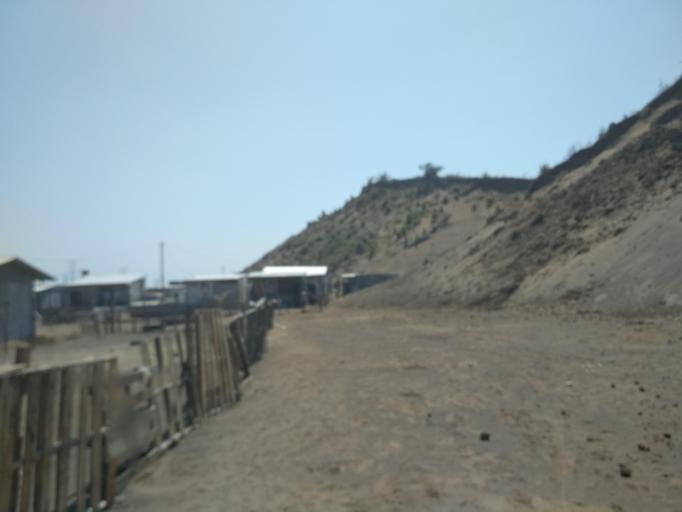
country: MX
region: Veracruz
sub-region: Veracruz
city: Lomas de Rio Medio Cuatro
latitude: 19.1897
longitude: -96.1980
